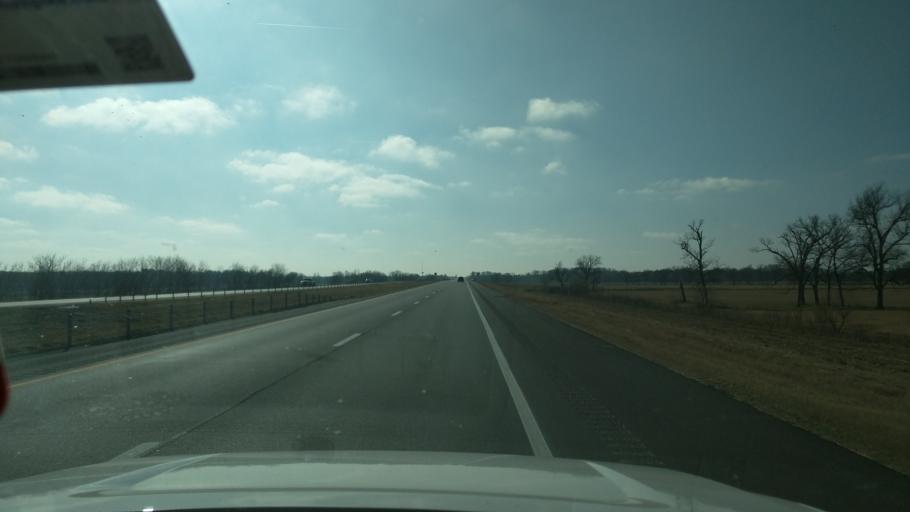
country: US
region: Oklahoma
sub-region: Washington County
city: Bartlesville
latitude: 36.6597
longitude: -95.9356
